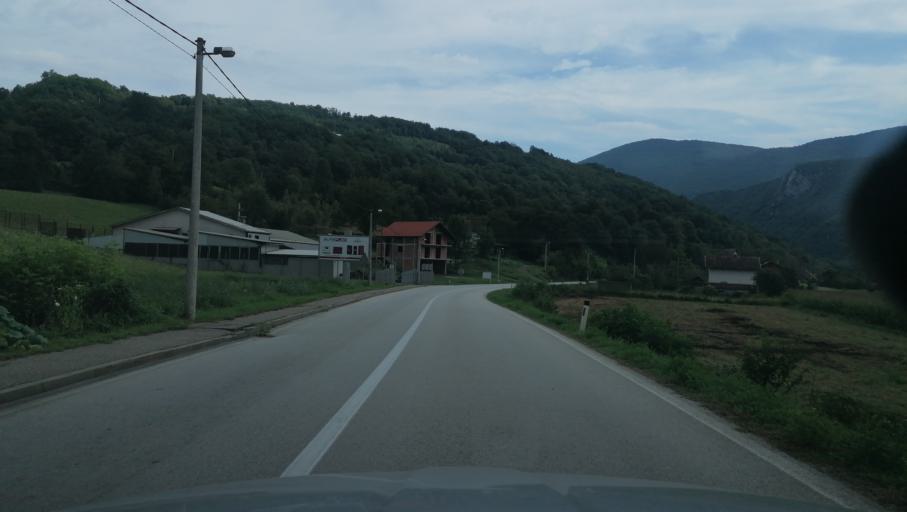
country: BA
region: Republika Srpska
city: Hiseti
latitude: 44.6194
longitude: 17.1456
